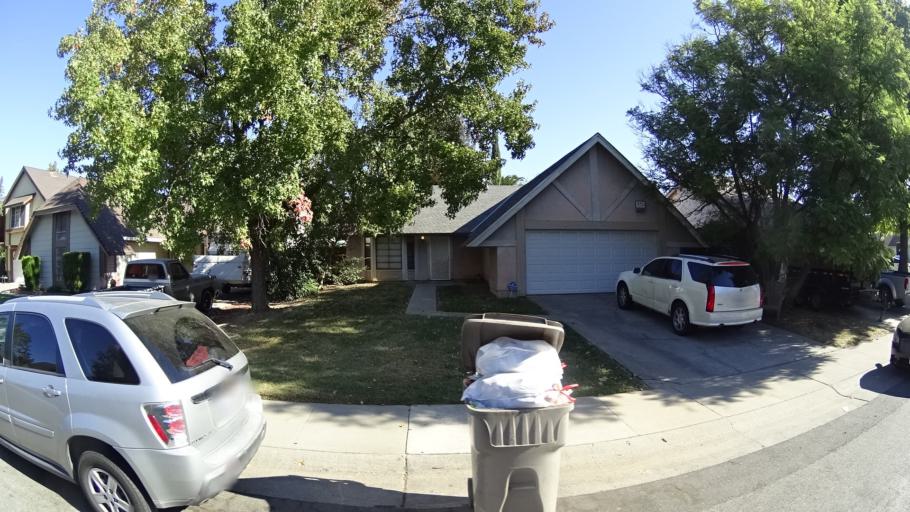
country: US
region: California
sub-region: Sacramento County
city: Florin
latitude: 38.4612
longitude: -121.4256
